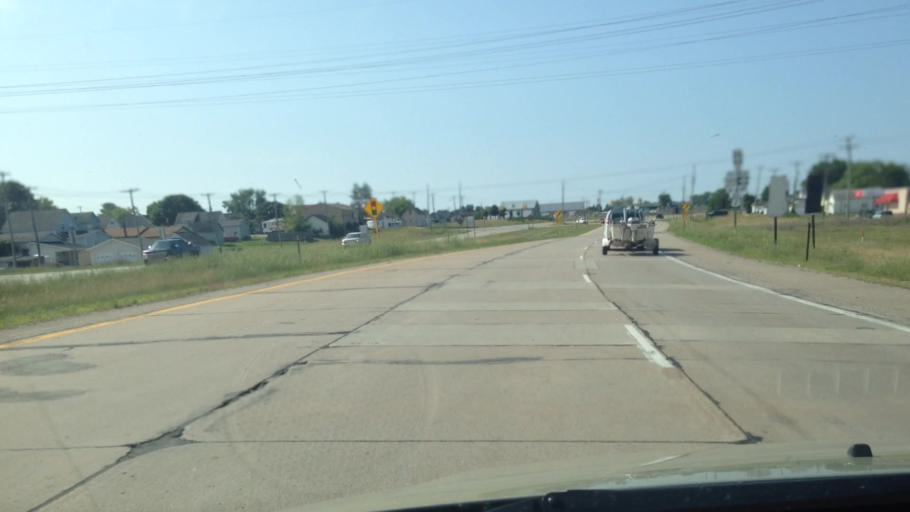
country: US
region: Michigan
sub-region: Delta County
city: Gladstone
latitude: 45.8550
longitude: -87.0234
